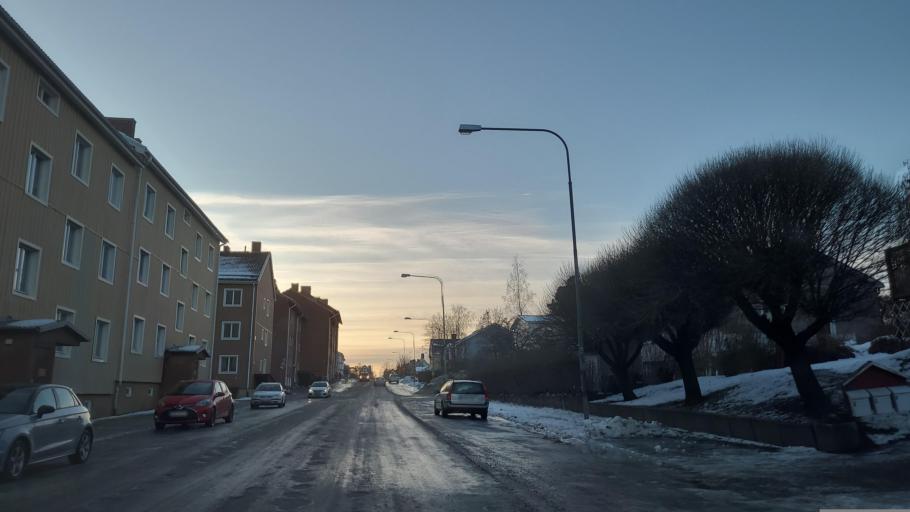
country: SE
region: Gaevleborg
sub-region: Soderhamns Kommun
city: Soderhamn
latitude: 61.3074
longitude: 17.0558
